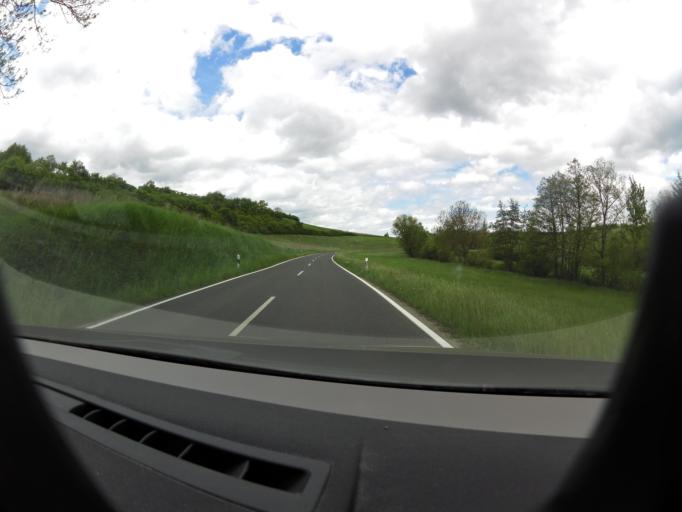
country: DE
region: Bavaria
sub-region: Regierungsbezirk Unterfranken
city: Dettelbach
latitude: 49.8245
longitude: 10.1498
